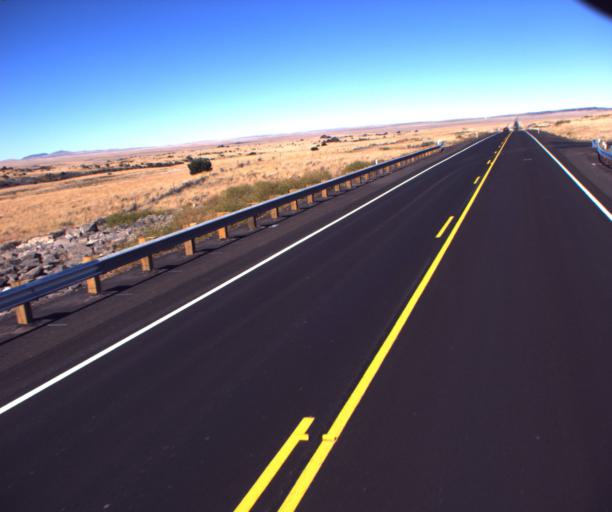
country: US
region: Arizona
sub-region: Apache County
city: Springerville
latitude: 34.2414
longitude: -109.3464
